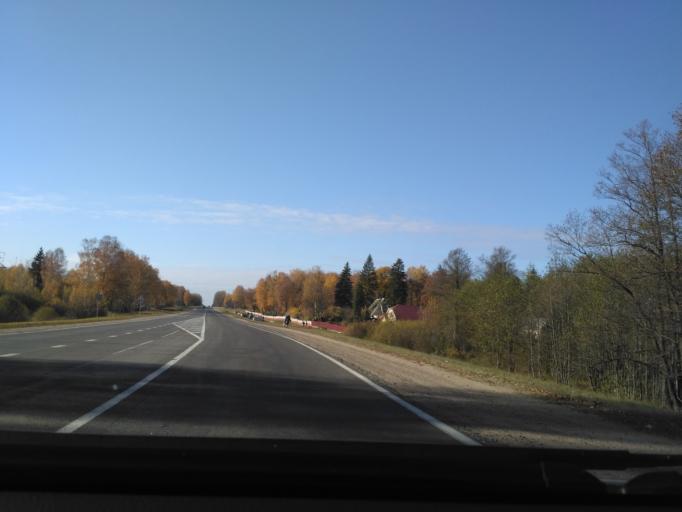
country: BY
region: Minsk
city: Horad Barysaw
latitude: 54.2552
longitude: 28.5712
